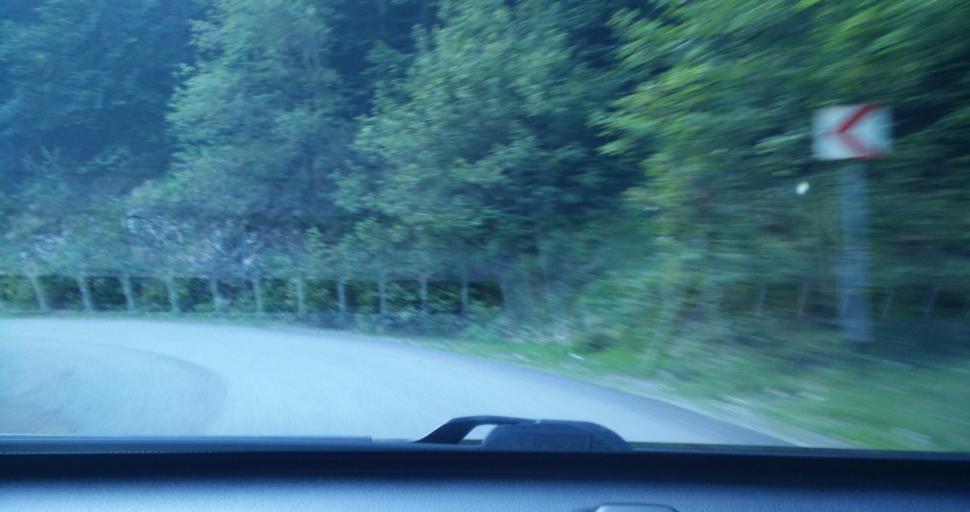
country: RO
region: Bihor
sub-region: Oras Nucet
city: Nucet
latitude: 46.5148
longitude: 22.6313
